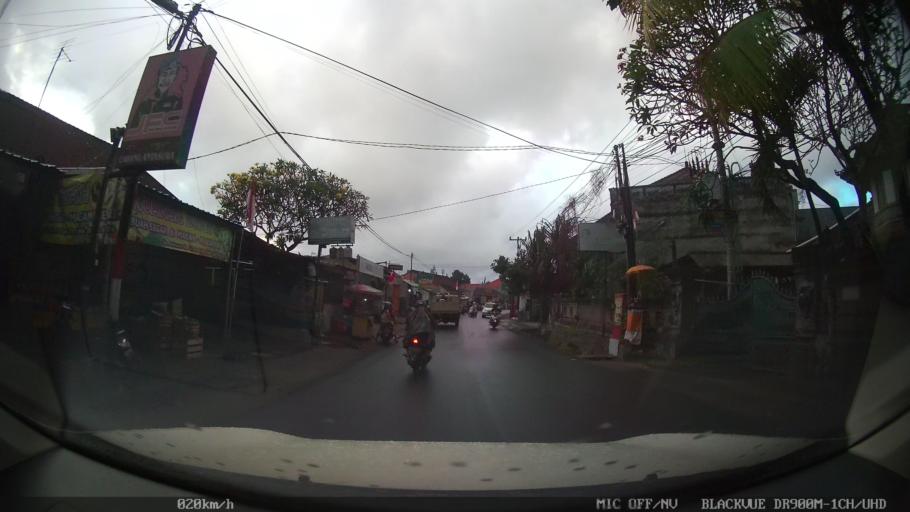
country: ID
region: Bali
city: Banjar Kayangan
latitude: -8.6212
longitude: 115.2234
